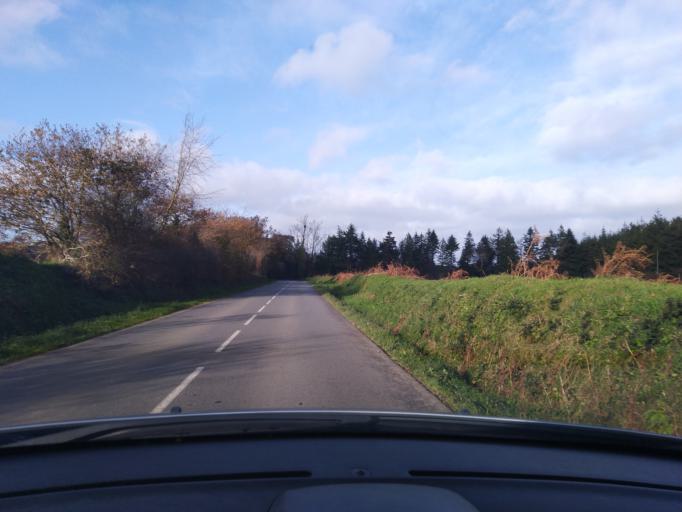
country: FR
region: Brittany
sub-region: Departement du Finistere
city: Plouigneau
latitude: 48.5496
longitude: -3.6850
